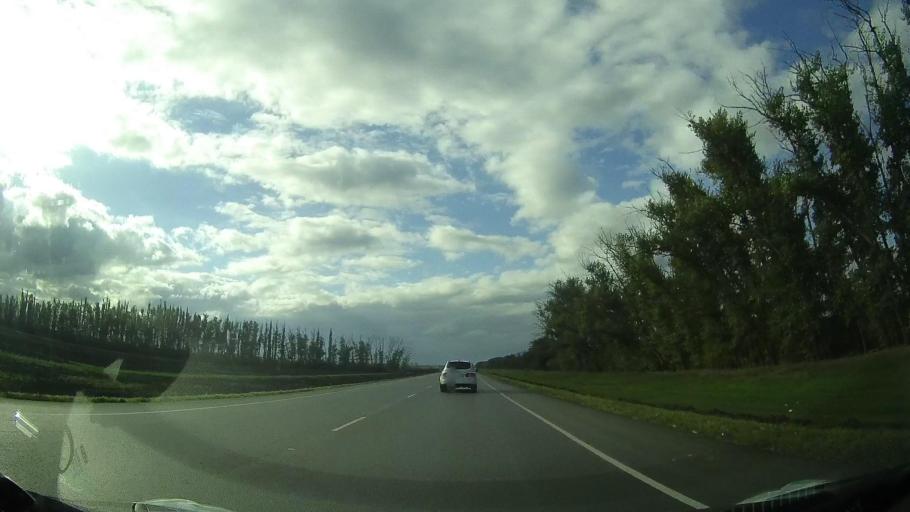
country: RU
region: Rostov
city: Tselina
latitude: 46.5312
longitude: 40.9404
